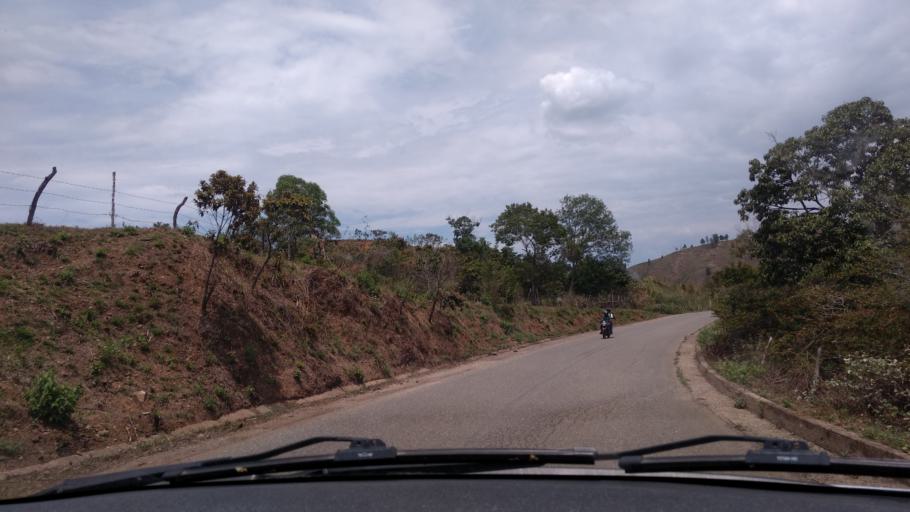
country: CO
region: Cauca
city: Buenos Aires
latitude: 3.0480
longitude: -76.6611
